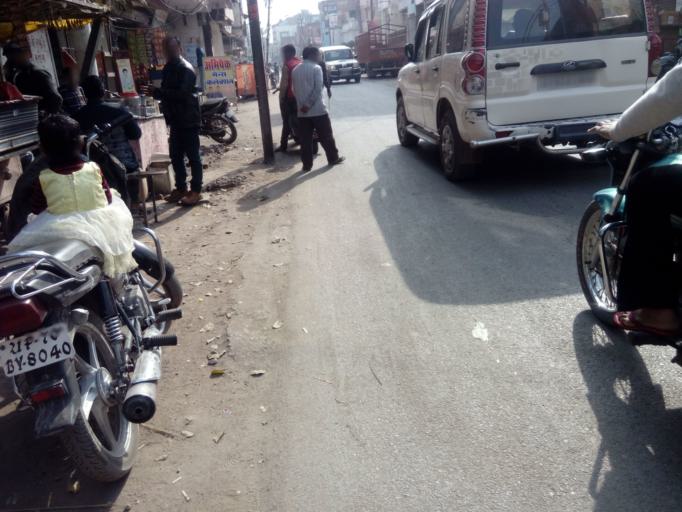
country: IN
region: Uttar Pradesh
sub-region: Allahabad
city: Allahabad
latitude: 25.4353
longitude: 81.8461
